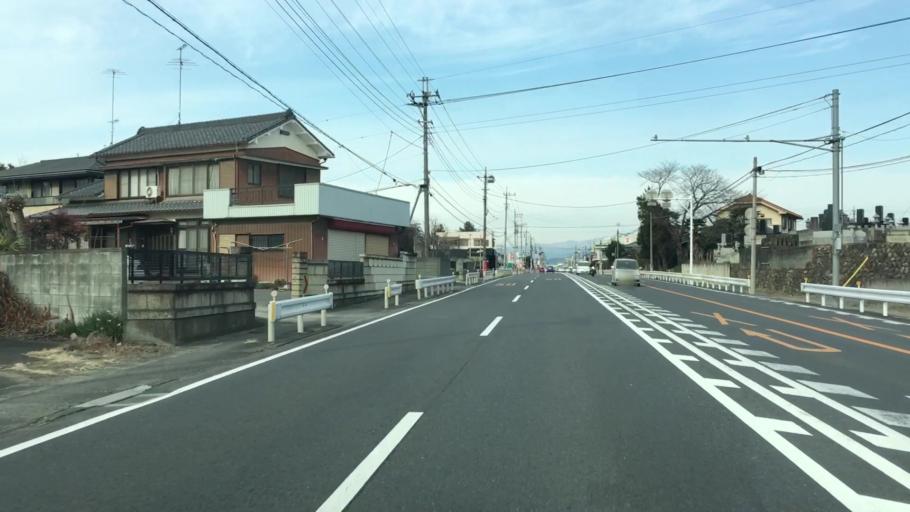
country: JP
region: Saitama
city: Menuma
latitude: 36.2475
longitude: 139.3795
